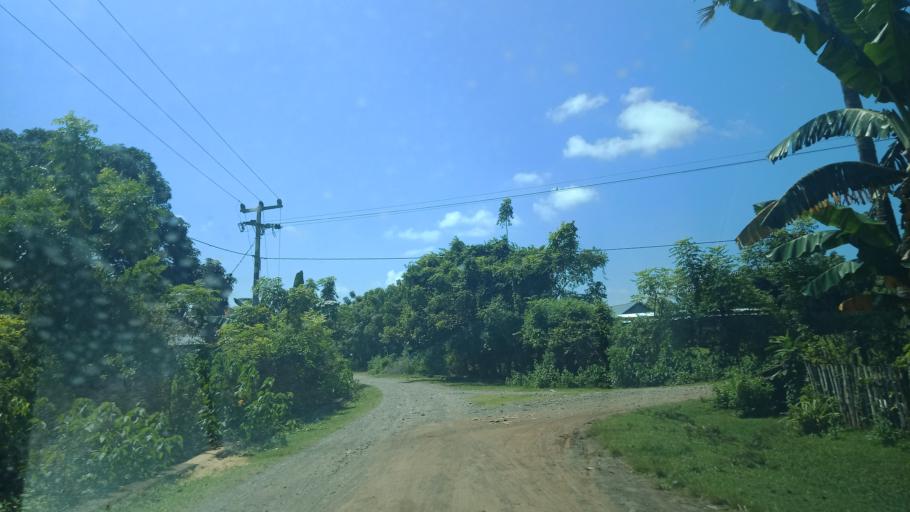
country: ID
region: South Sulawesi
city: Kadai
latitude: -4.7694
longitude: 120.3726
